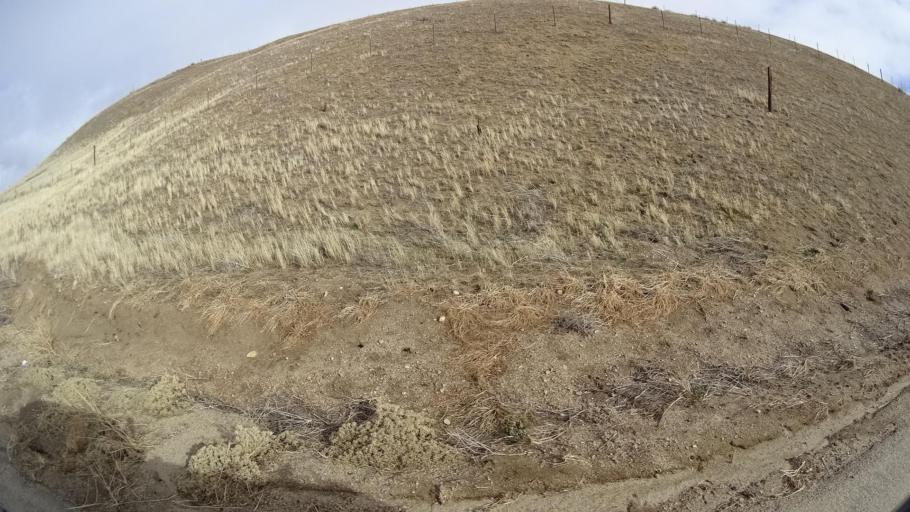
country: US
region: California
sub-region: Kern County
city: Maricopa
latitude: 34.9029
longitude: -119.3734
